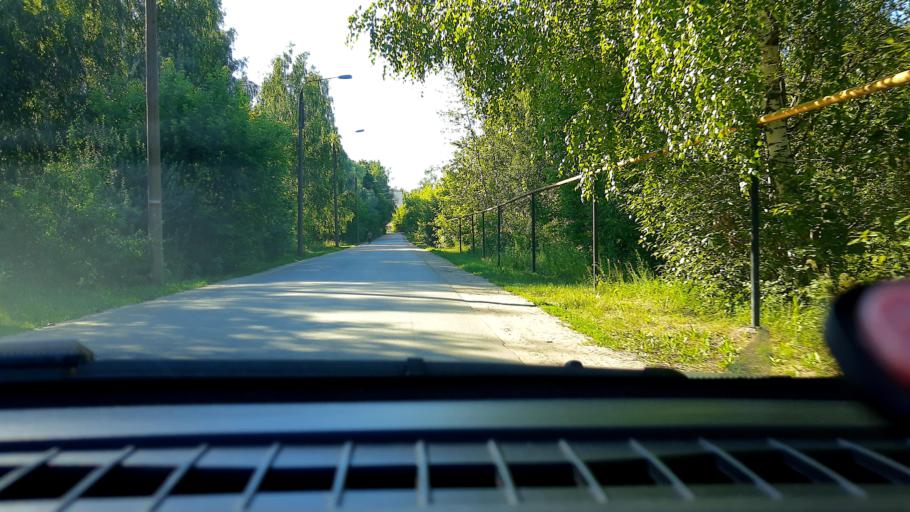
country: RU
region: Nizjnij Novgorod
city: Burevestnik
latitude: 56.1985
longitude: 43.8138
